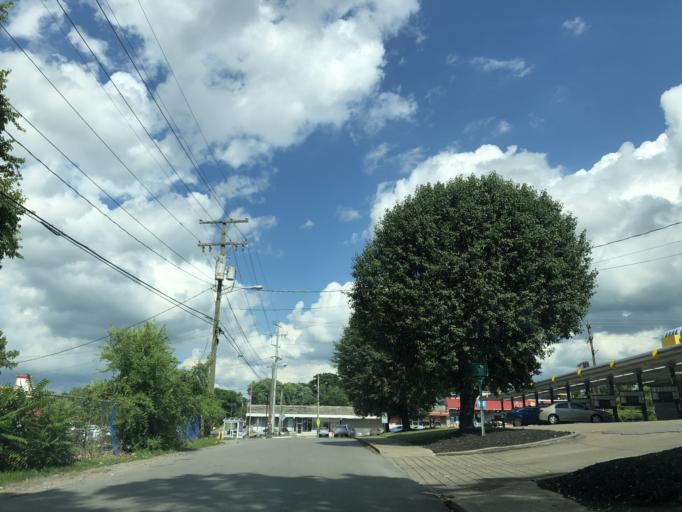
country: US
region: Tennessee
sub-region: Davidson County
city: Nashville
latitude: 36.2084
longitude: -86.7684
